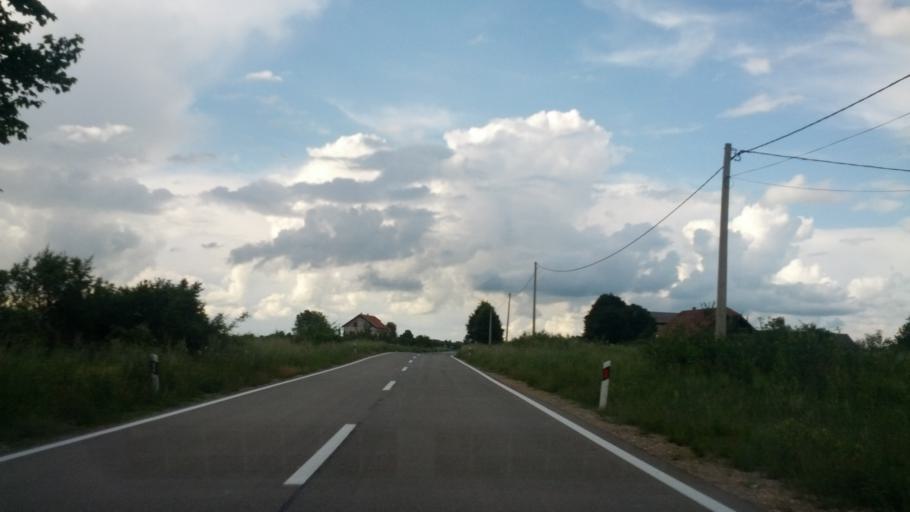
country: BA
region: Federation of Bosnia and Herzegovina
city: Izacic
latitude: 44.8927
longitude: 15.7240
